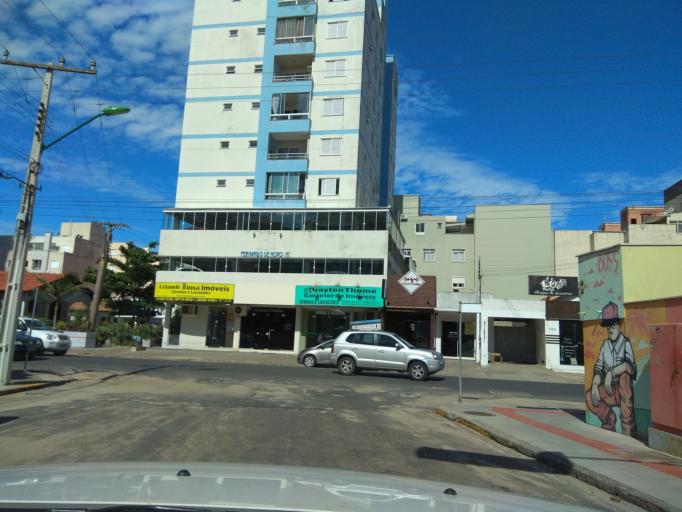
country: BR
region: Santa Catarina
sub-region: Laguna
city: Laguna
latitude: -28.4785
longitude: -48.7692
